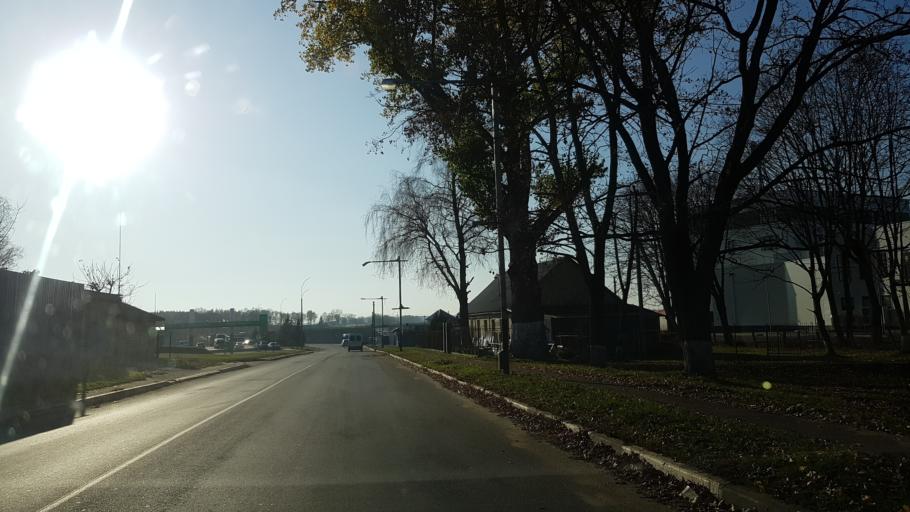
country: BY
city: Fanipol
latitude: 53.7373
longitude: 27.3106
